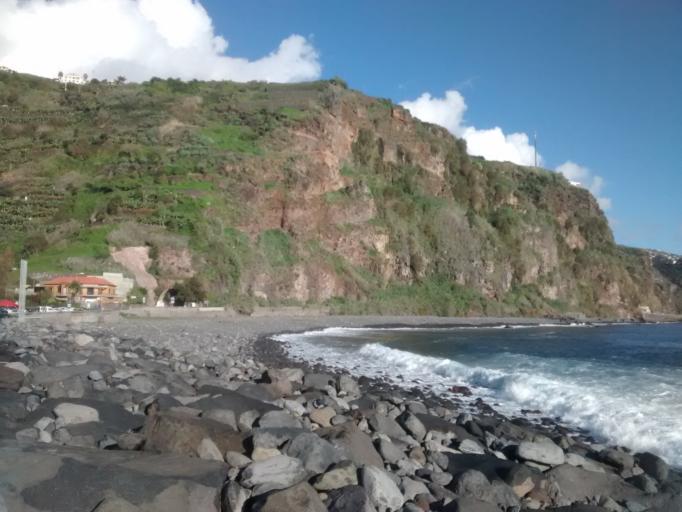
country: PT
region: Madeira
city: Ponta do Sol
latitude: 32.6790
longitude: -17.0882
